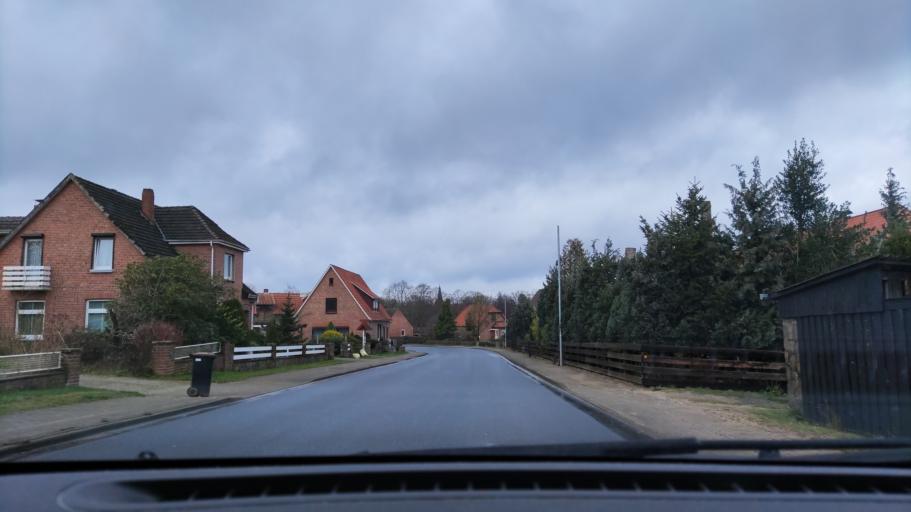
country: DE
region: Lower Saxony
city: Hanstedt Eins
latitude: 53.0425
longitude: 10.3787
